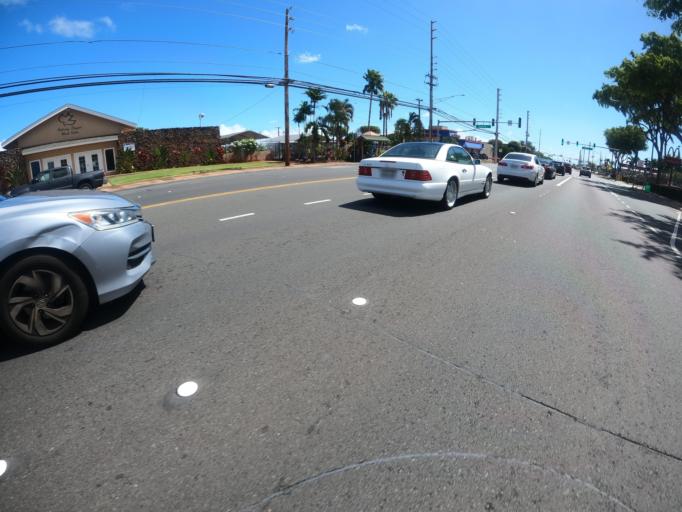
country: US
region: Hawaii
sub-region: Honolulu County
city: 'Ewa Beach
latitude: 21.3178
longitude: -158.0138
